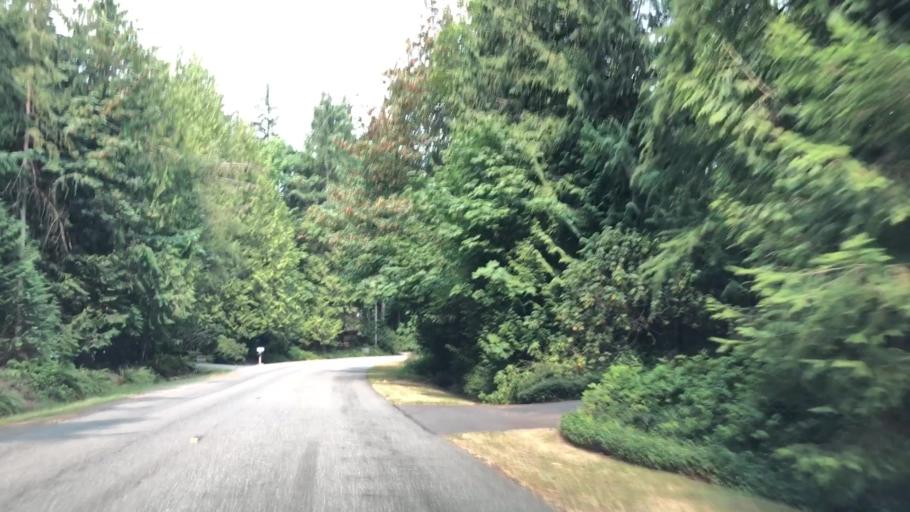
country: US
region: Washington
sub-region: King County
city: Cottage Lake
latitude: 47.7661
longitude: -122.0786
